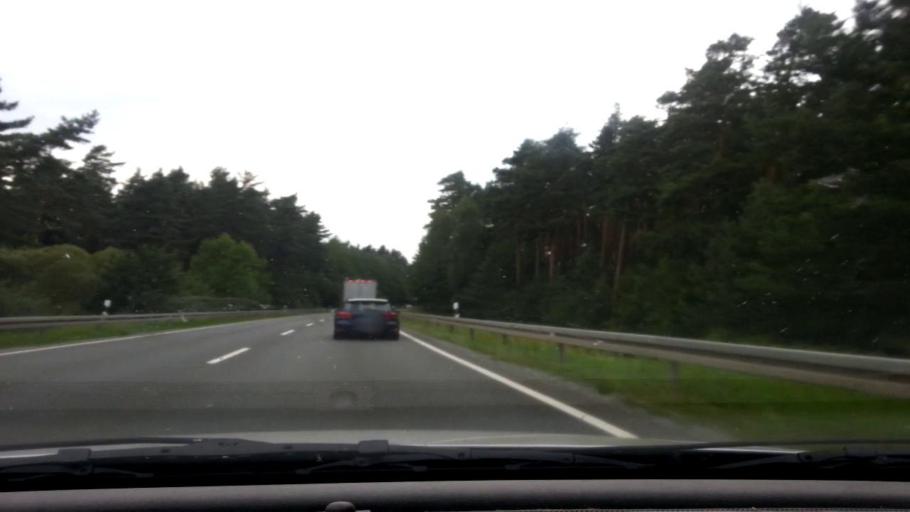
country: DE
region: Bavaria
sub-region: Upper Franconia
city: Seybothenreuth
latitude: 49.8878
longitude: 11.7191
